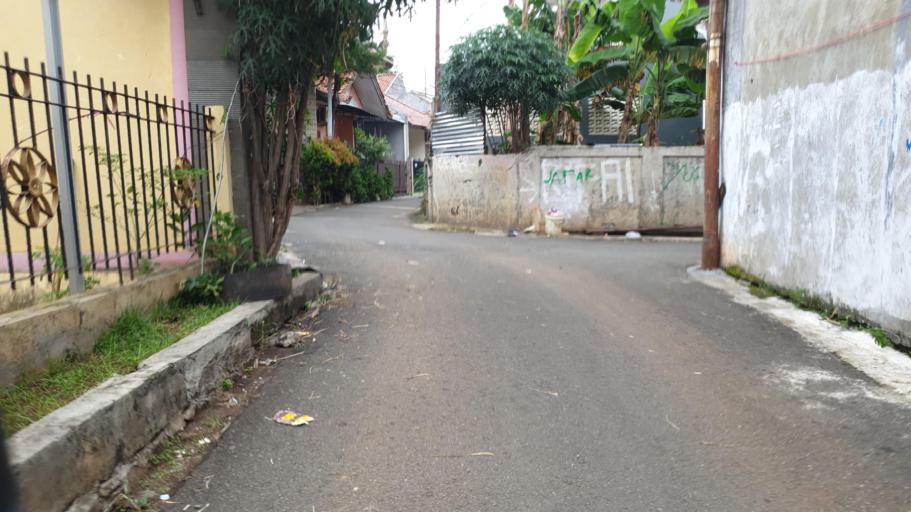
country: ID
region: West Java
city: Depok
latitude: -6.3338
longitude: 106.8215
